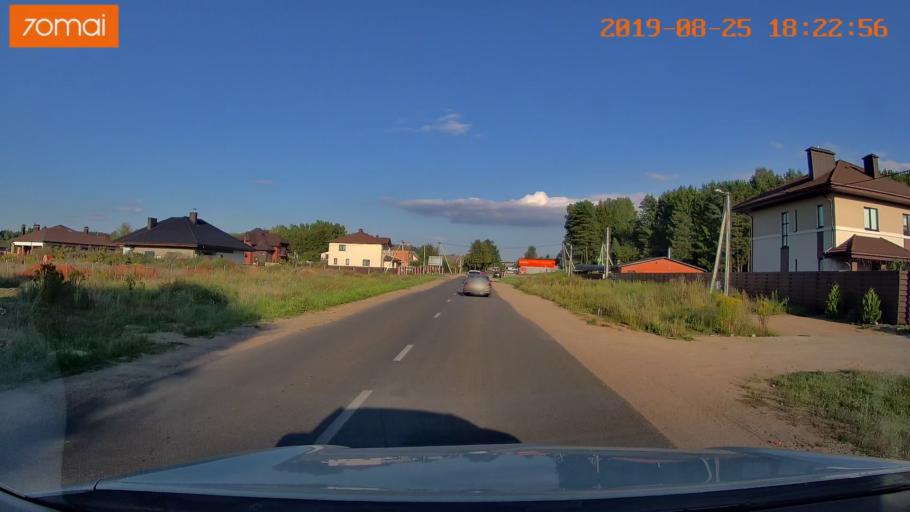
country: BY
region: Minsk
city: Khatsyezhyna
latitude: 53.9398
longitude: 27.3245
